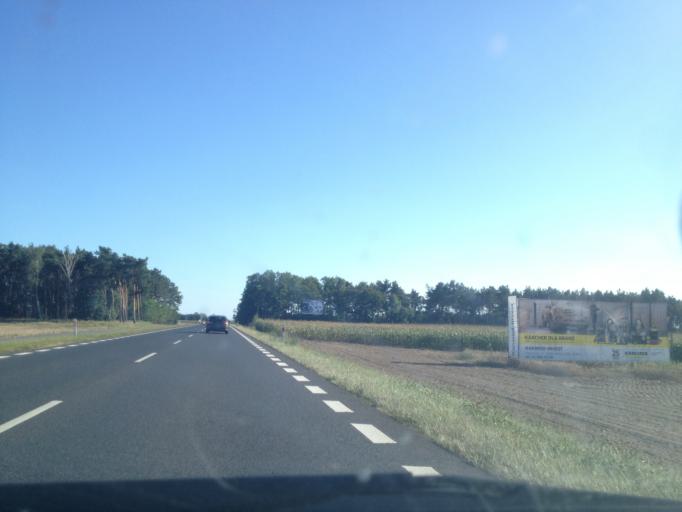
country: PL
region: Greater Poland Voivodeship
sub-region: Powiat sremski
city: Srem
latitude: 52.1169
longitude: 17.0436
